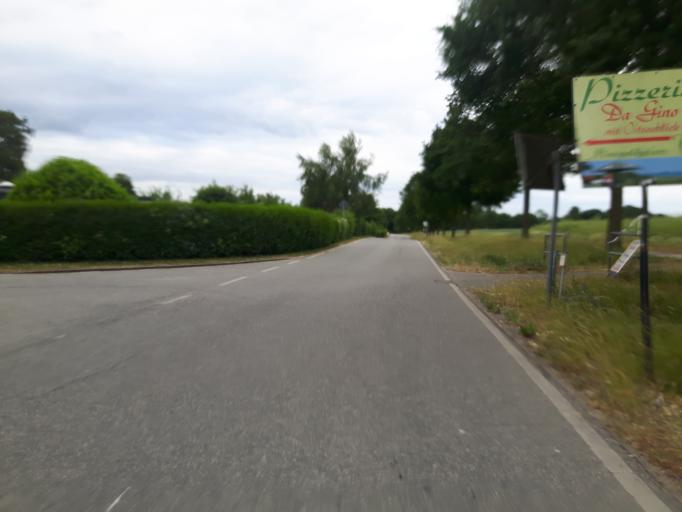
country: DE
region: Schleswig-Holstein
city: Schashagen
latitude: 54.1048
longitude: 10.8956
